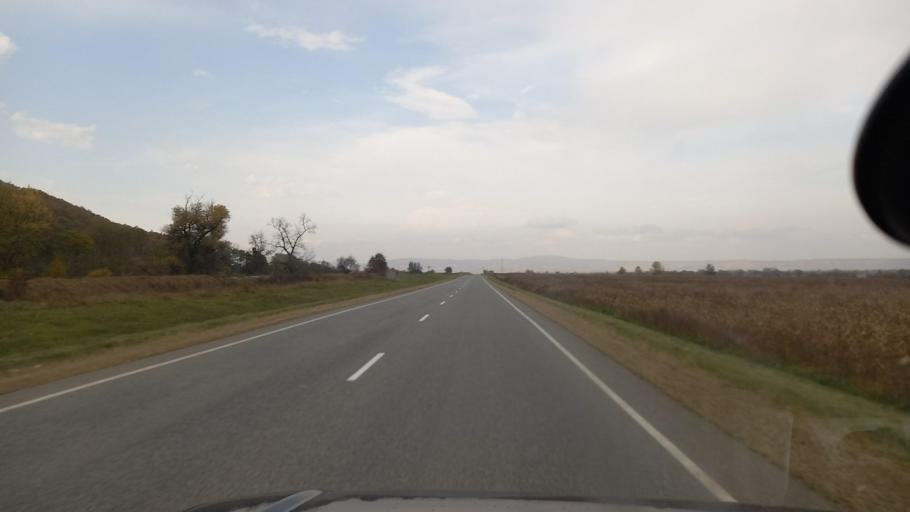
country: RU
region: Krasnodarskiy
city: Shedok
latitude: 44.2436
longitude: 40.8615
